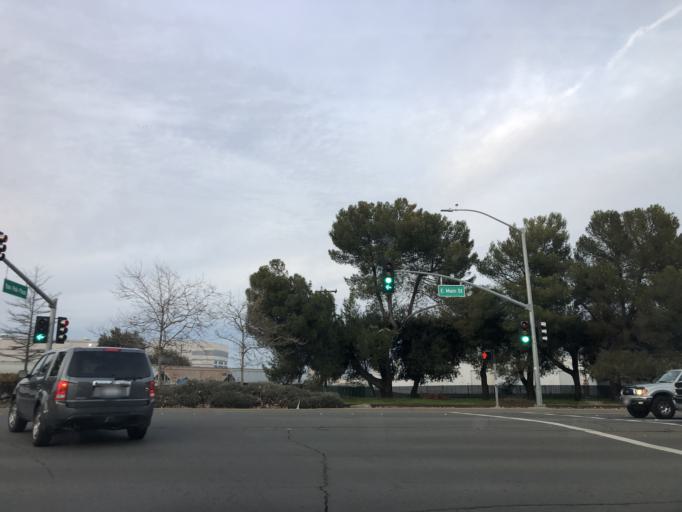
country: US
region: California
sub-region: Yolo County
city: Woodland
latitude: 38.6770
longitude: -121.7394
